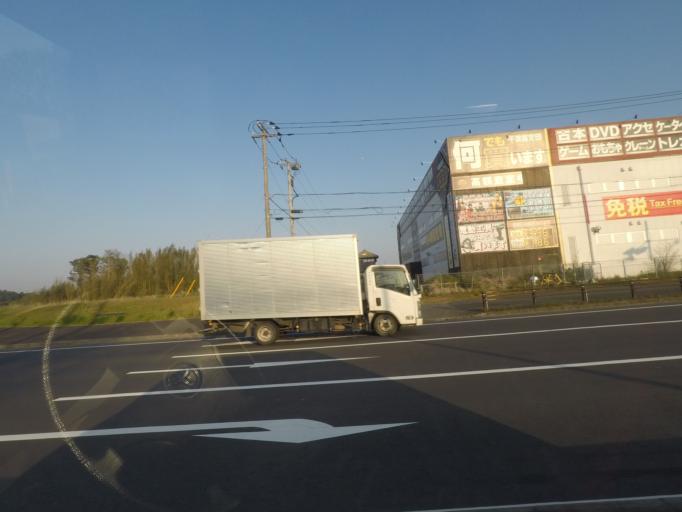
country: JP
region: Chiba
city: Shisui
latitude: 35.7177
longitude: 140.2621
